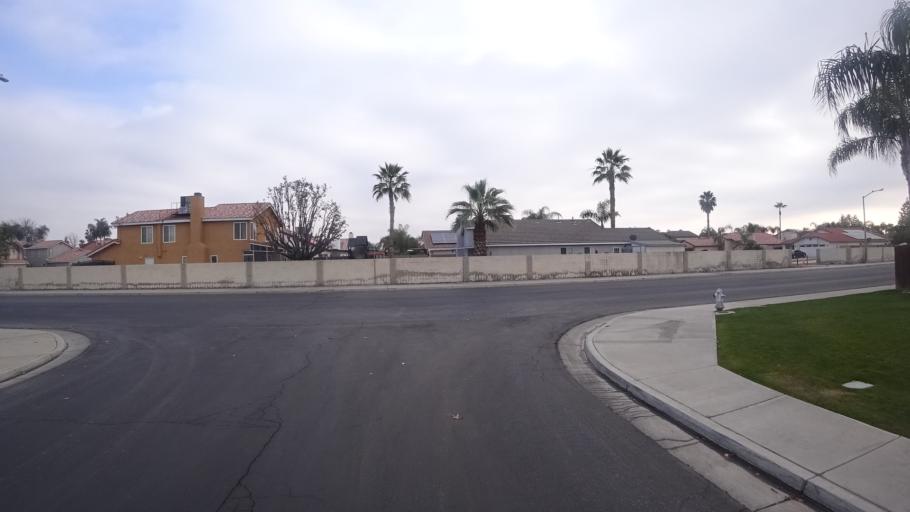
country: US
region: California
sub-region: Kern County
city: Greenfield
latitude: 35.3024
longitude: -119.0728
